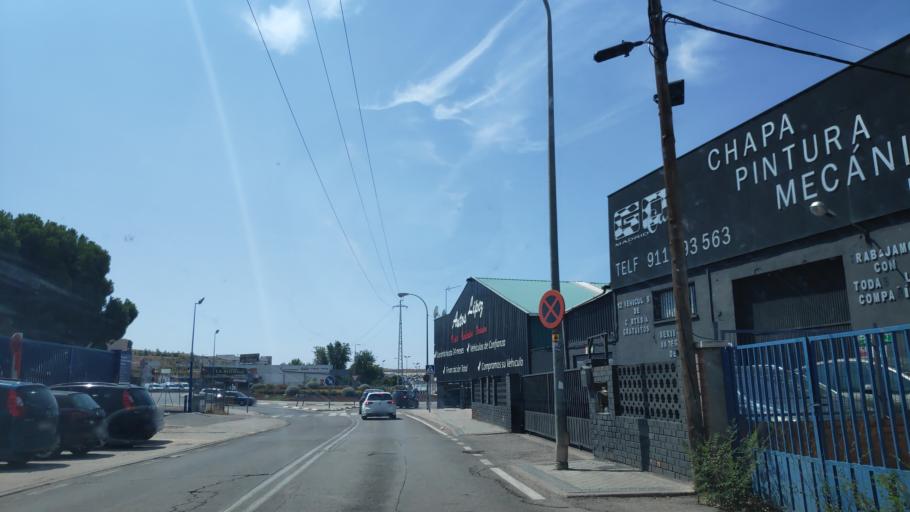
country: ES
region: Madrid
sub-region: Provincia de Madrid
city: Arganda
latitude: 40.3053
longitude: -3.4534
